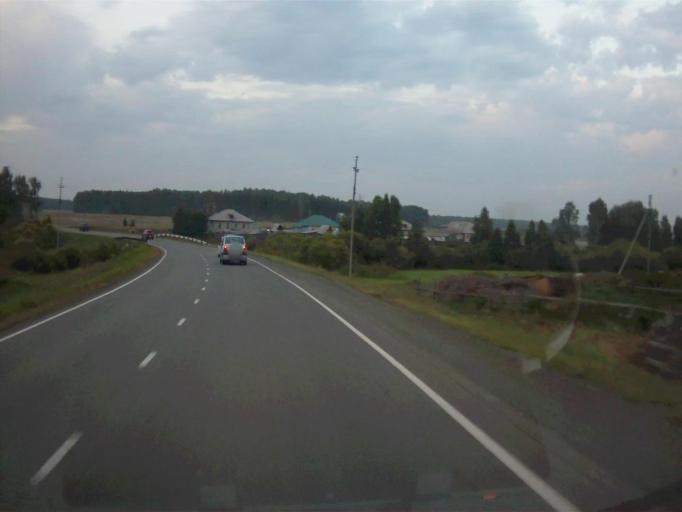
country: RU
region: Chelyabinsk
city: Chebarkul'
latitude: 55.1806
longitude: 60.4755
